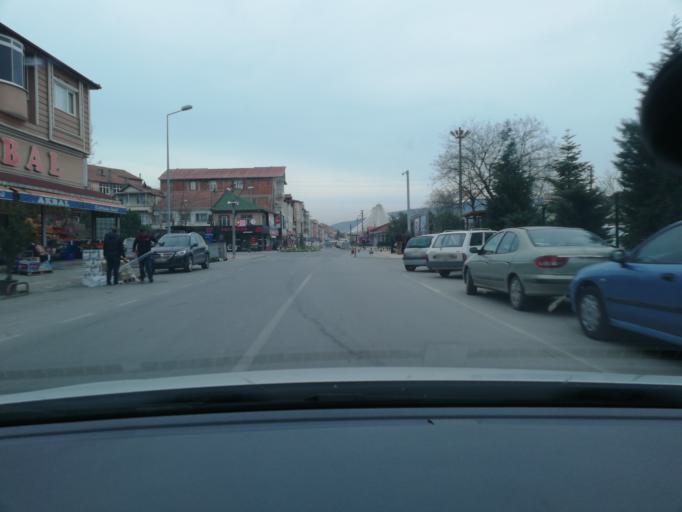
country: TR
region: Zonguldak
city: Caycuma
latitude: 41.4238
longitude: 32.0947
